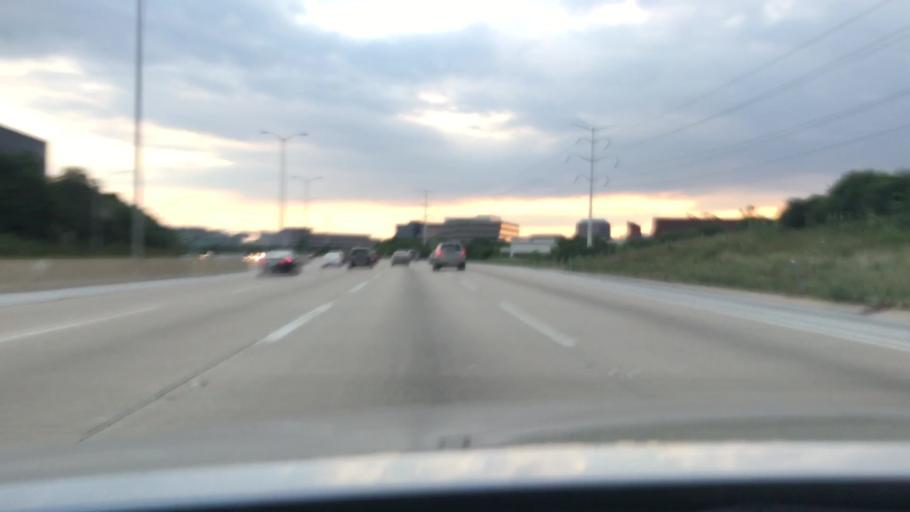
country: US
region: Illinois
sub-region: DuPage County
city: Downers Grove
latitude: 41.8328
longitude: -88.0133
